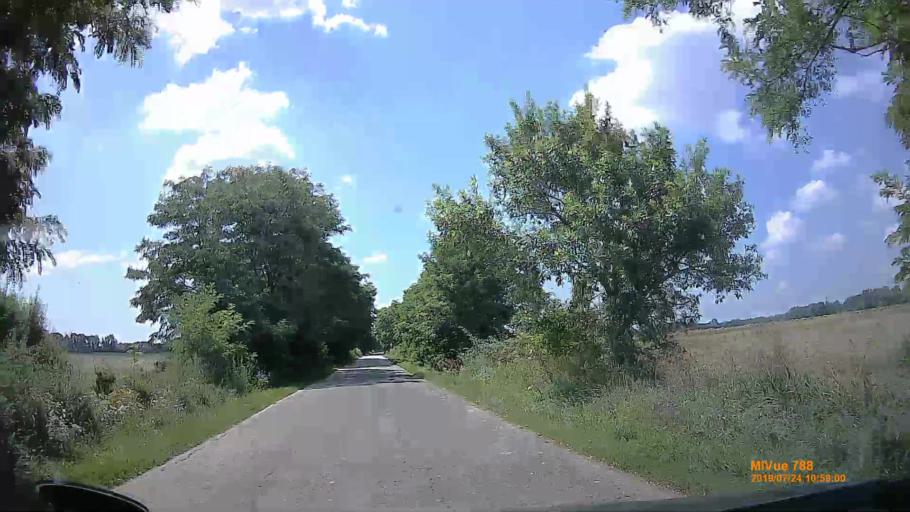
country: HU
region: Szabolcs-Szatmar-Bereg
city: Tarpa
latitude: 48.1711
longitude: 22.5164
